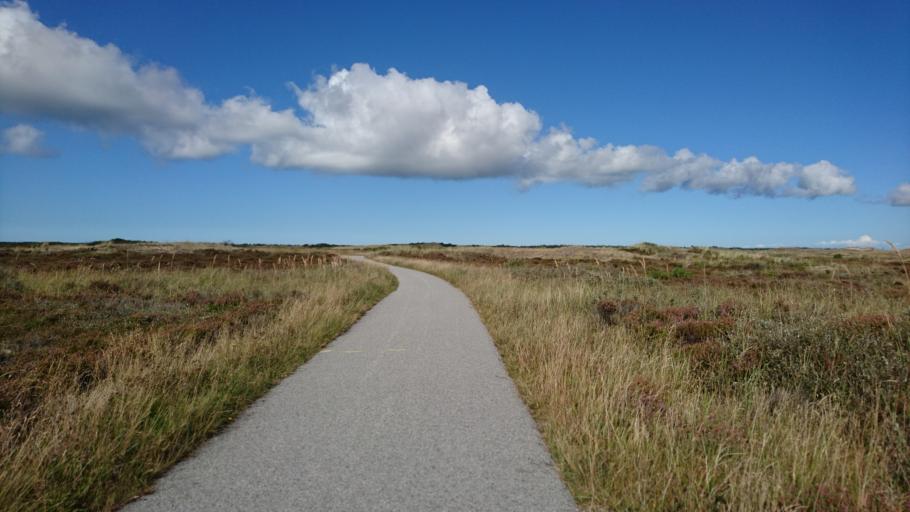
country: DK
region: North Denmark
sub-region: Frederikshavn Kommune
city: Skagen
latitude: 57.6833
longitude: 10.5032
